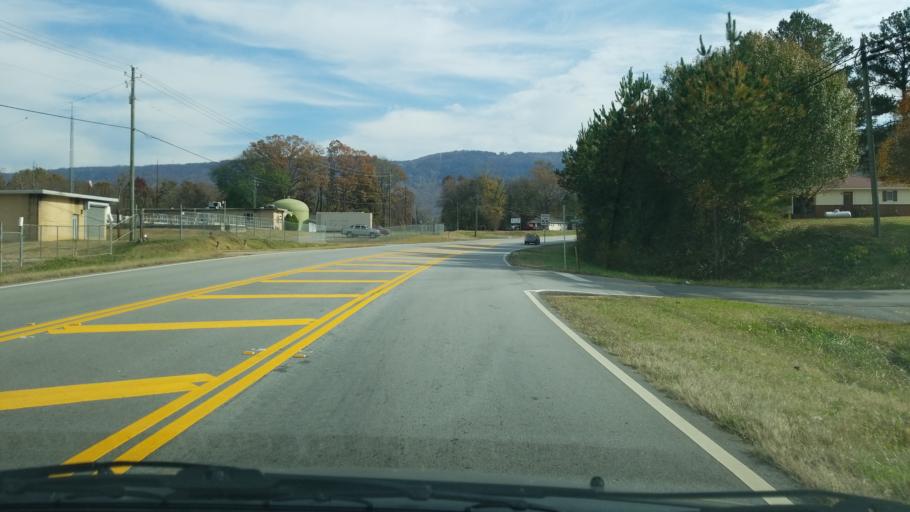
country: US
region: Georgia
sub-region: Dade County
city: Trenton
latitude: 34.8628
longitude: -85.4994
